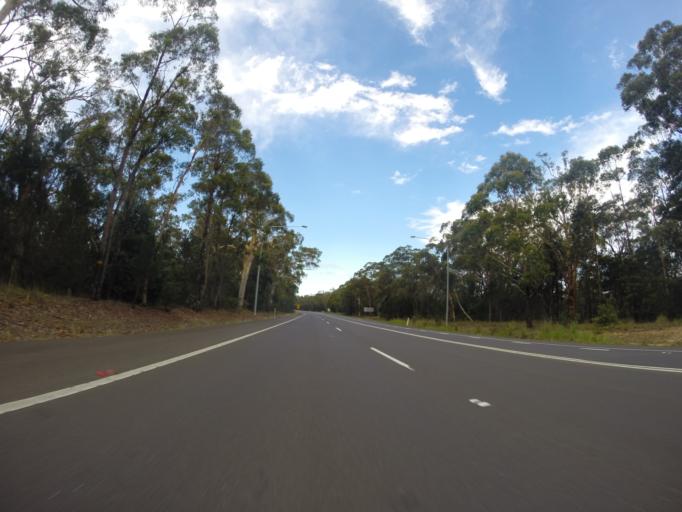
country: AU
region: New South Wales
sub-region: Shoalhaven Shire
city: Falls Creek
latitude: -35.1089
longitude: 150.4921
